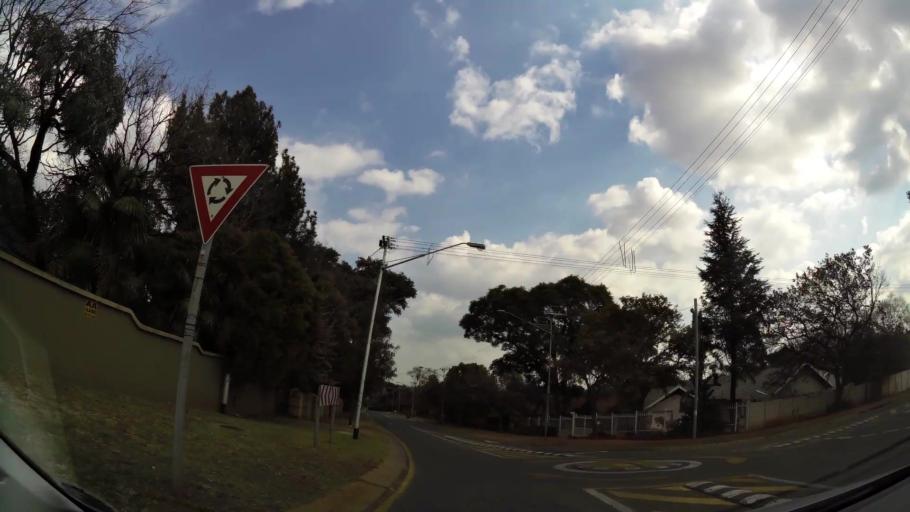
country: ZA
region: Gauteng
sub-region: City of Tshwane Metropolitan Municipality
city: Pretoria
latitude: -25.7491
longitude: 28.3117
